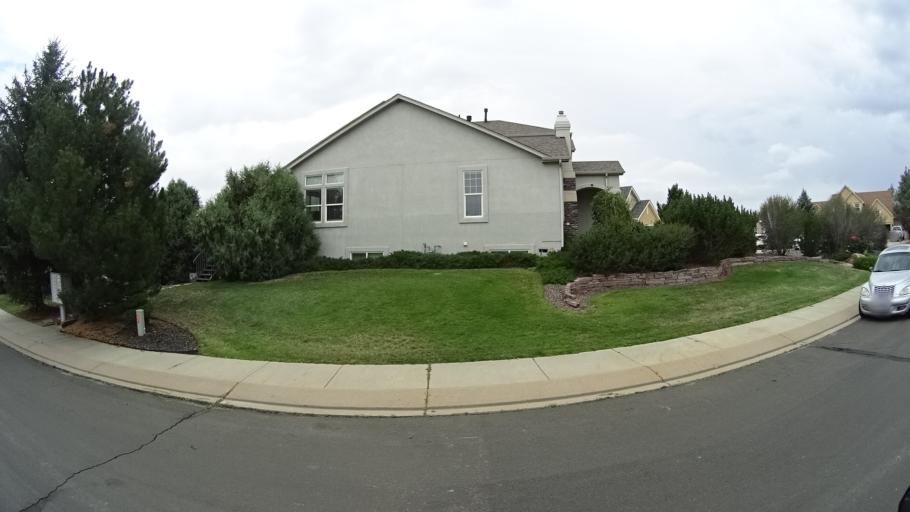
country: US
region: Colorado
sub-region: El Paso County
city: Gleneagle
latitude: 39.0050
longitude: -104.7911
